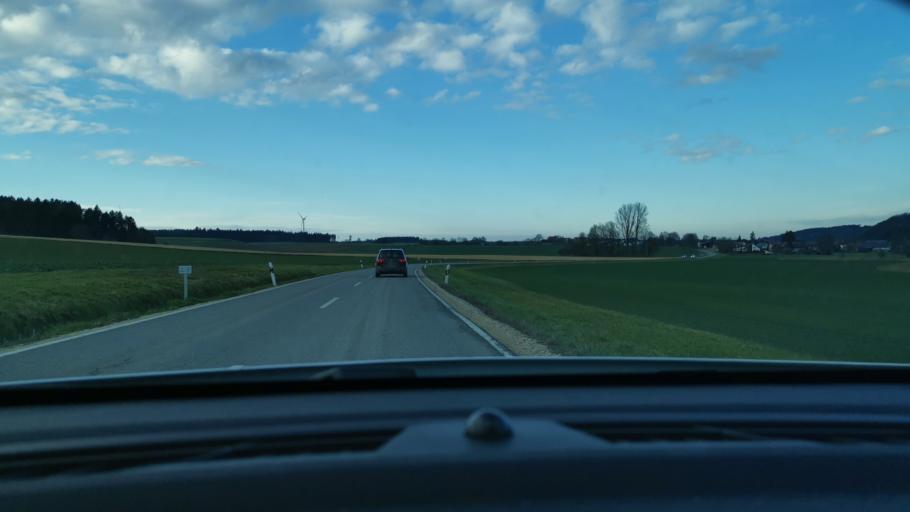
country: DE
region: Bavaria
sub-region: Swabia
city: Holzheim
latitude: 48.5767
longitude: 10.9672
